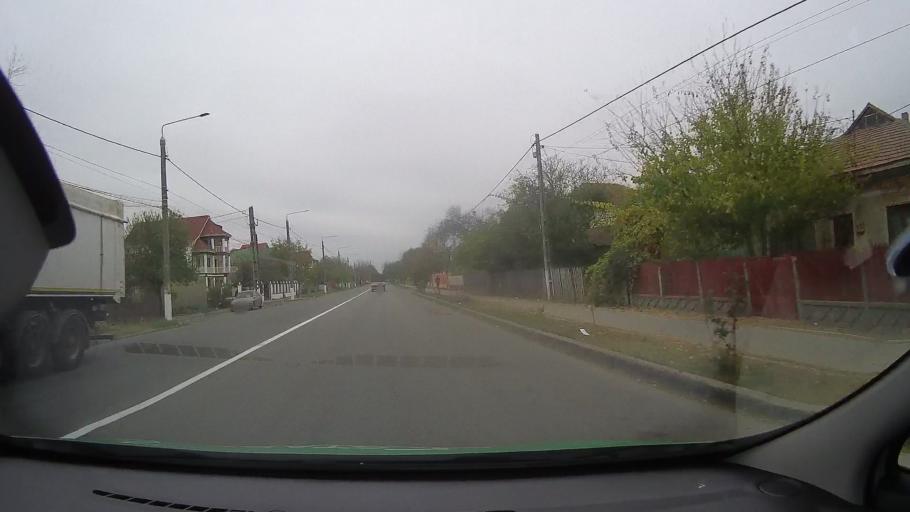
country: RO
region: Ialomita
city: Tandarei
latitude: 44.6400
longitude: 27.6698
